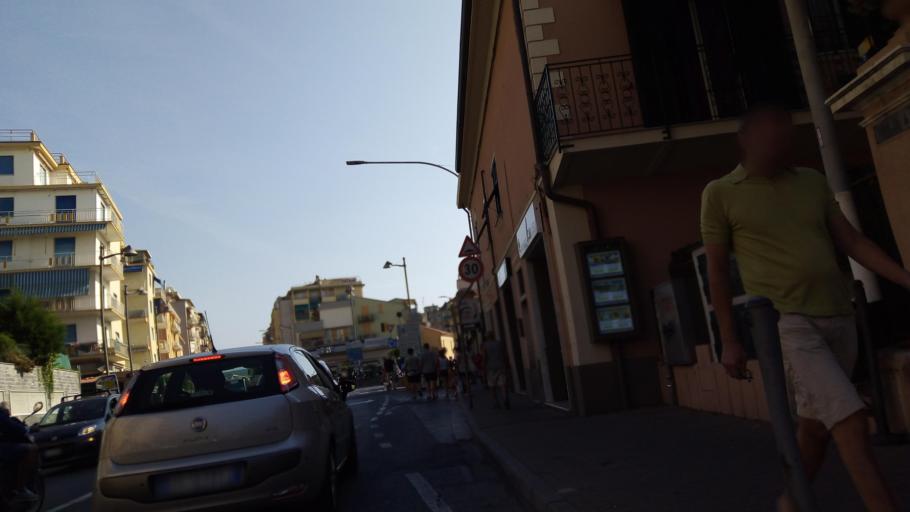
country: IT
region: Liguria
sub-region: Provincia di Savona
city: Loano
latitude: 44.1230
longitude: 8.2536
